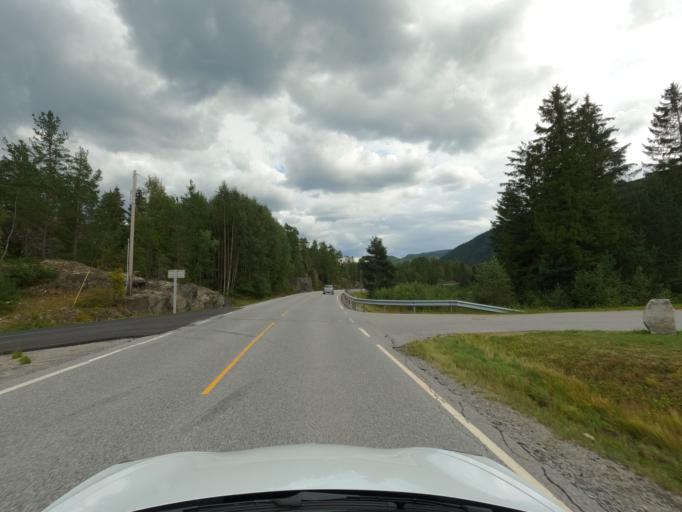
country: NO
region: Telemark
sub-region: Hjartdal
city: Sauland
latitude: 59.8616
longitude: 8.9387
